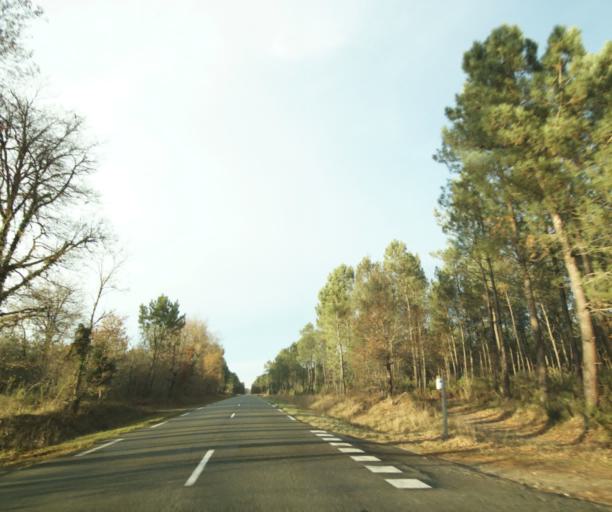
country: FR
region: Aquitaine
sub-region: Departement des Landes
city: Gabarret
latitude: 44.0387
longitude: -0.0344
